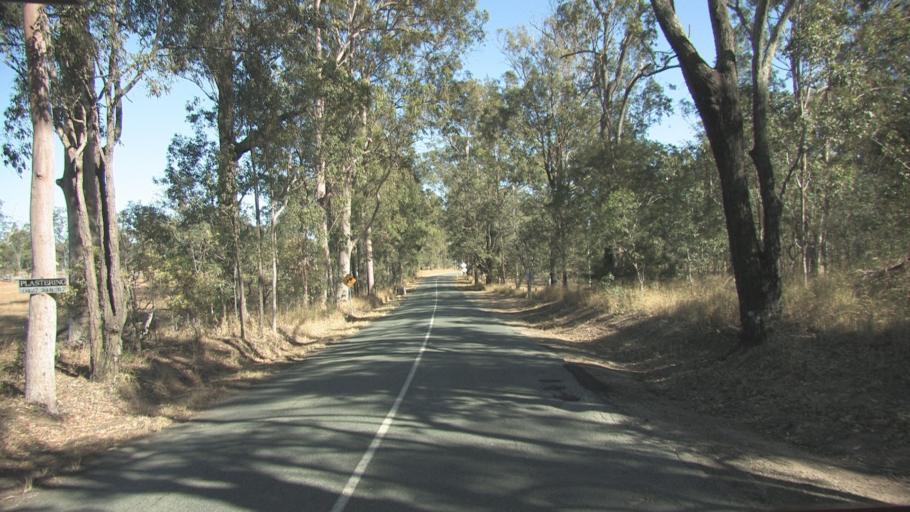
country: AU
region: Queensland
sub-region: Logan
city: Cedar Vale
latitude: -27.8636
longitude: 152.9973
